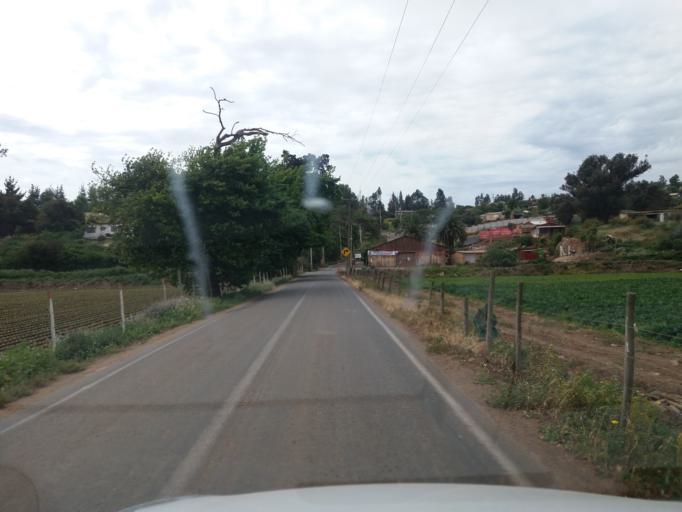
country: CL
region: Valparaiso
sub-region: Provincia de Marga Marga
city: Villa Alemana
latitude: -32.9162
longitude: -71.3952
